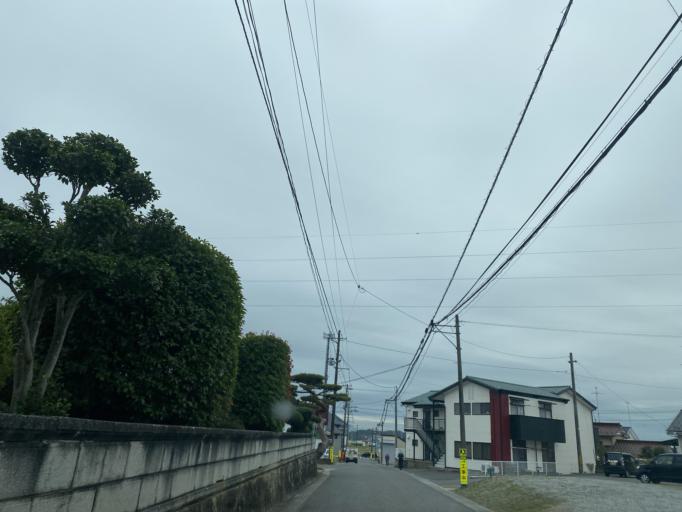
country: JP
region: Fukushima
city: Koriyama
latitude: 37.3749
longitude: 140.3367
